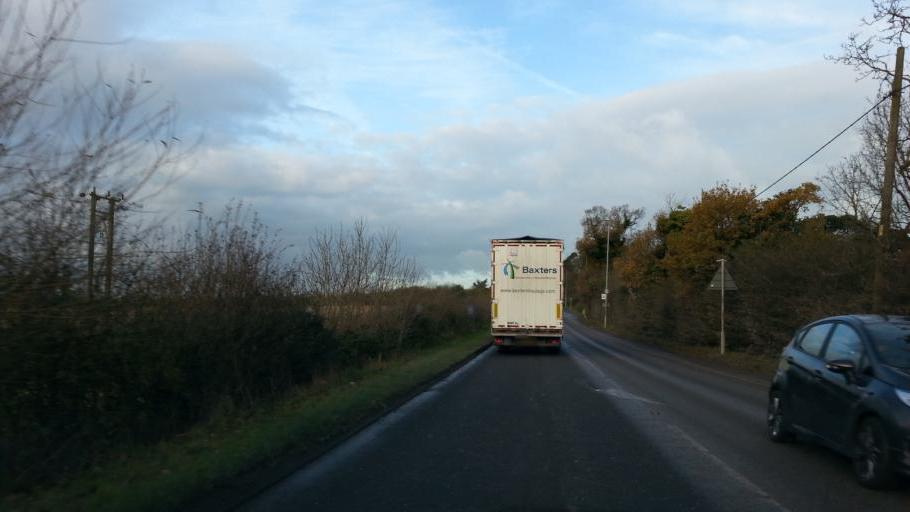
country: GB
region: England
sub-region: Leicestershire
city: Coalville
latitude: 52.7083
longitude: -1.3339
